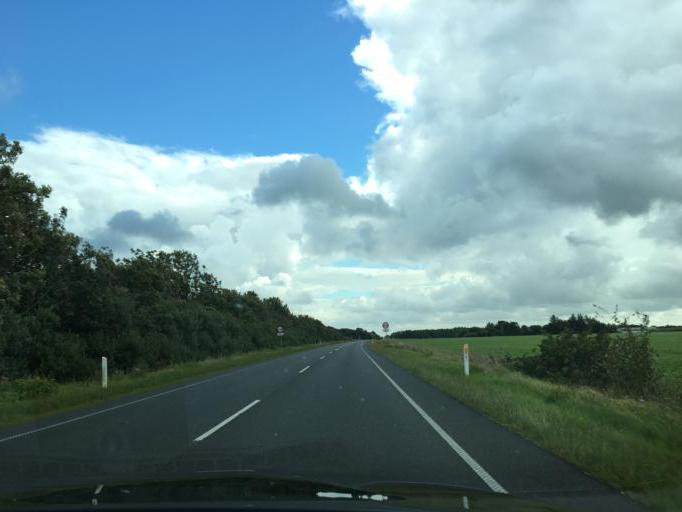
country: DK
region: South Denmark
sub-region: Varde Kommune
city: Olgod
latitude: 55.7804
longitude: 8.6244
